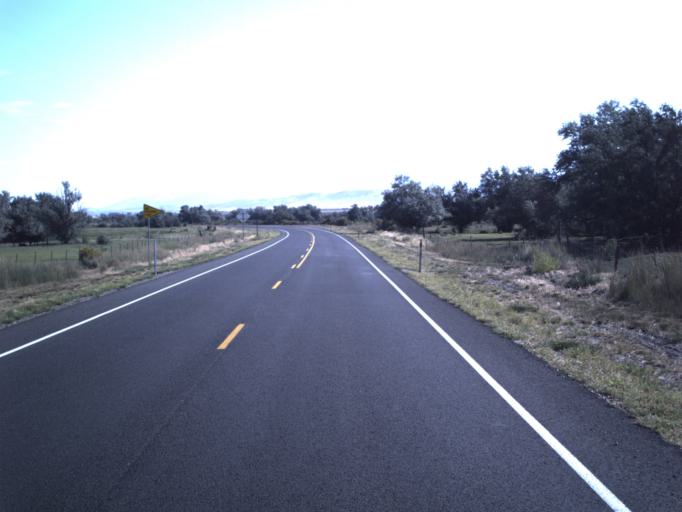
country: US
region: Utah
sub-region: Sevier County
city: Salina
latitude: 39.0095
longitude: -111.8570
